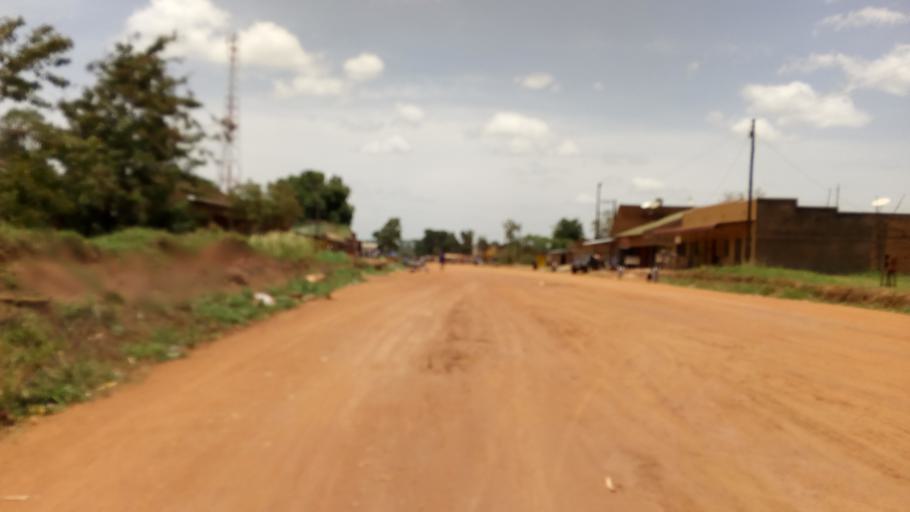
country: UG
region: Northern Region
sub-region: Gulu District
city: Gulu
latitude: 2.8182
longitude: 32.3399
